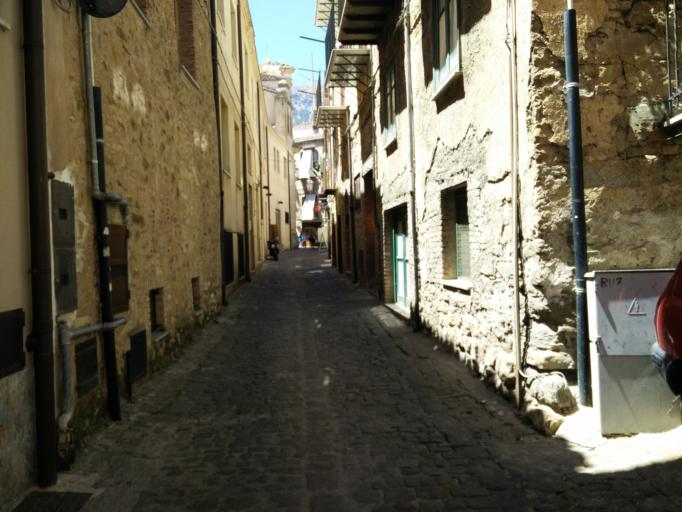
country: IT
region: Sicily
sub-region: Palermo
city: Castelbuono
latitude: 37.9323
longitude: 14.0880
